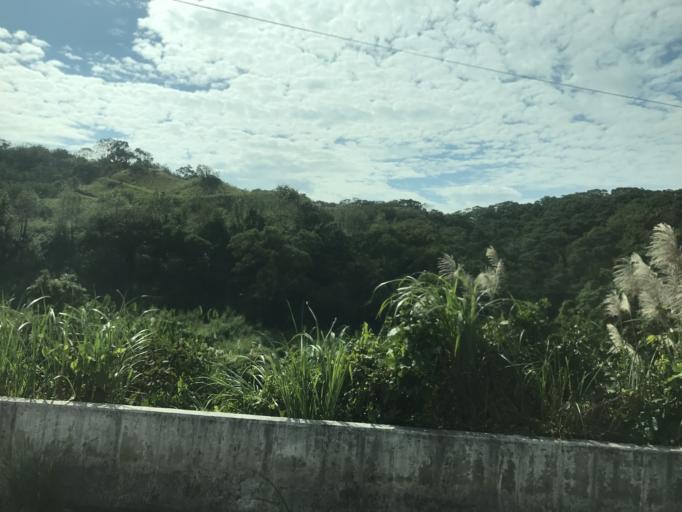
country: TW
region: Taiwan
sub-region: Hsinchu
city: Hsinchu
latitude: 24.7707
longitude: 120.9460
